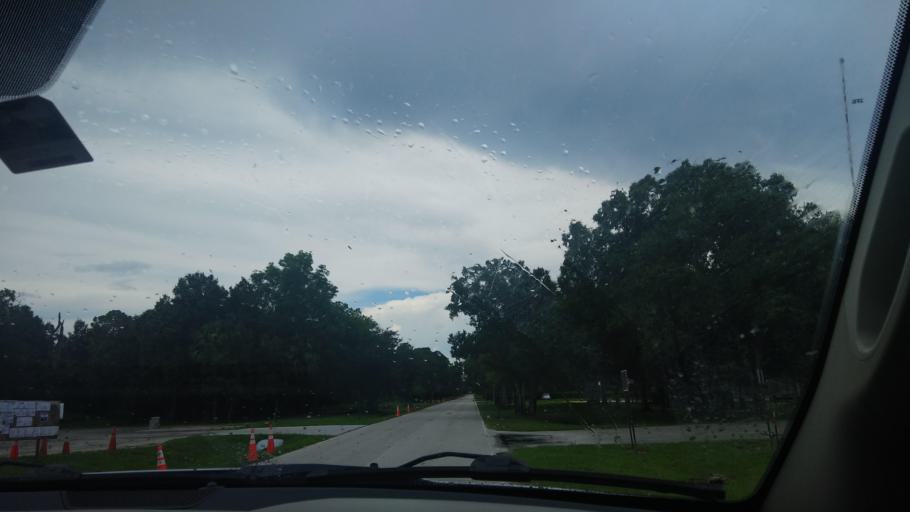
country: US
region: Florida
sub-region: Indian River County
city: Fellsmere
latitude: 27.7676
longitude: -80.6013
